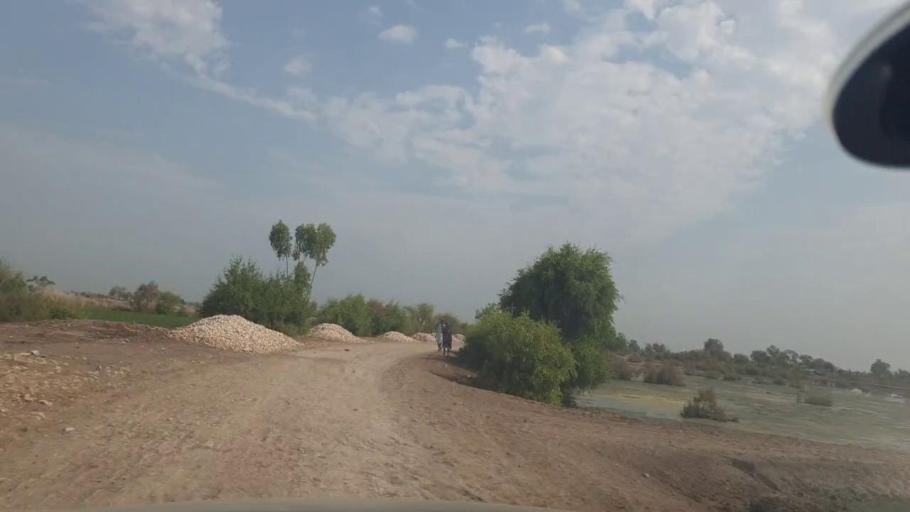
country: PK
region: Balochistan
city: Mehrabpur
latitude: 28.0745
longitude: 68.0995
